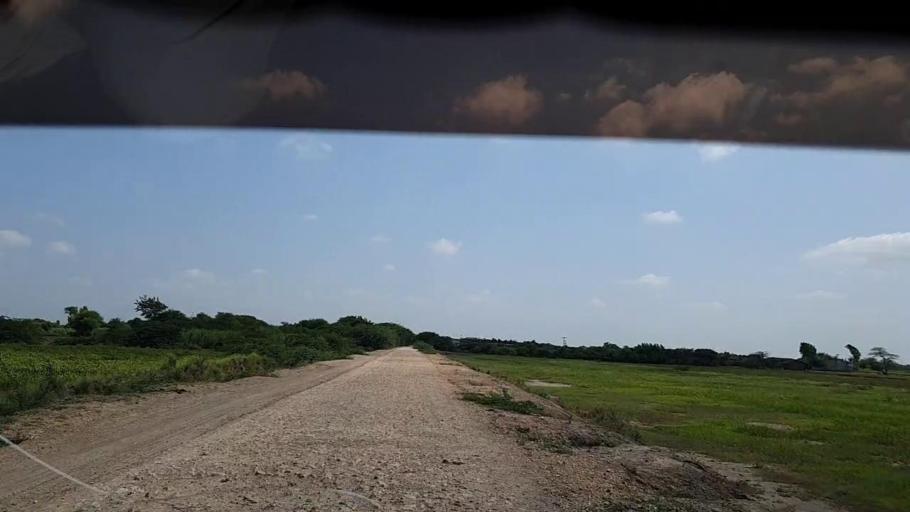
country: PK
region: Sindh
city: Kadhan
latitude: 24.6013
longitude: 68.9866
